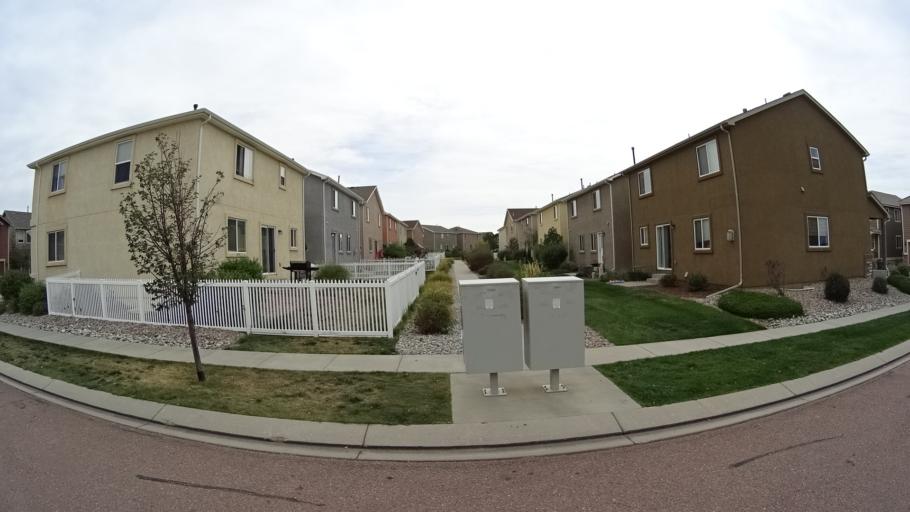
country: US
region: Colorado
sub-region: El Paso County
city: Cimarron Hills
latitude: 38.9174
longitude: -104.6855
